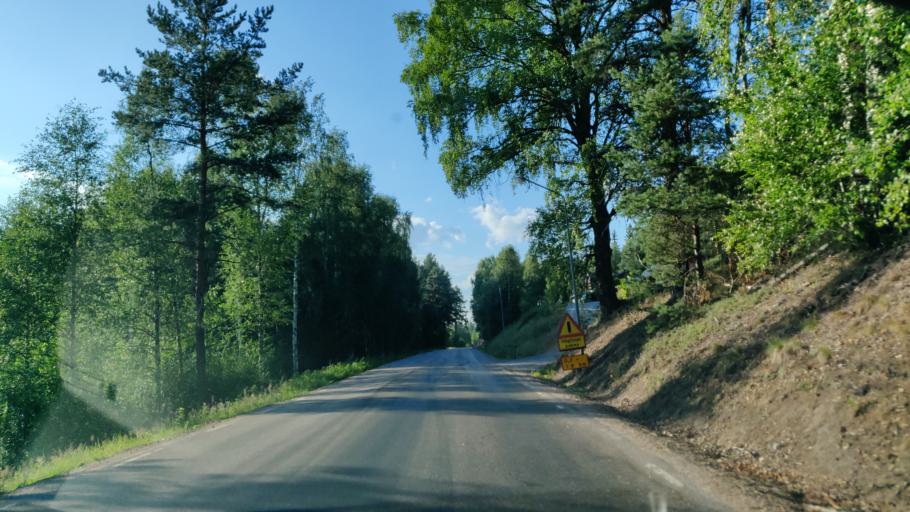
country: SE
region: Vaermland
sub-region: Hagfors Kommun
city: Ekshaerad
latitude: 60.1769
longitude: 13.5280
